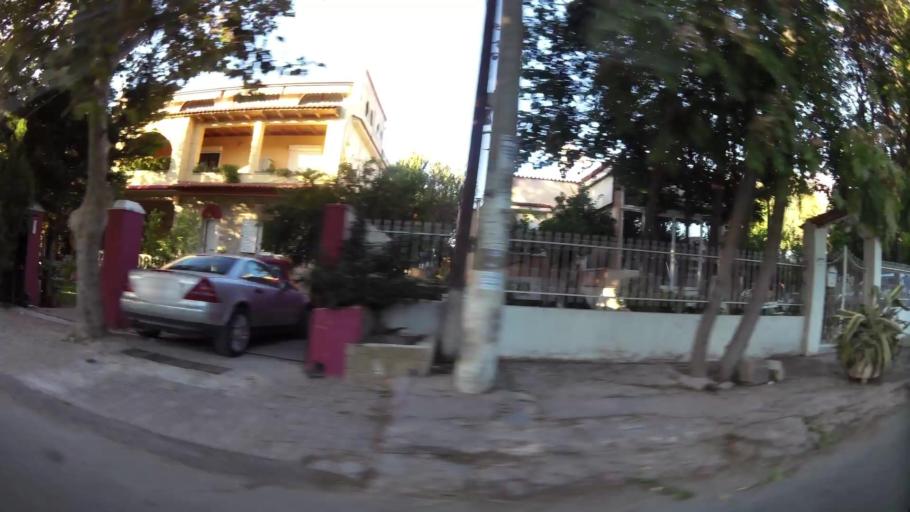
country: GR
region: Attica
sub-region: Nomarchia Athinas
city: Kifisia
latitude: 38.0743
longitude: 23.7979
